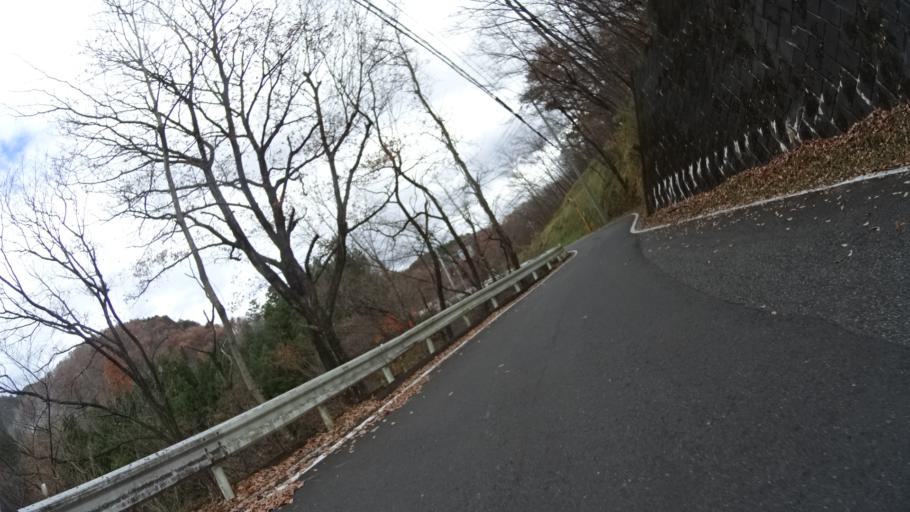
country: JP
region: Gunma
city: Omamacho-omama
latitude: 36.4942
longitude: 139.1840
